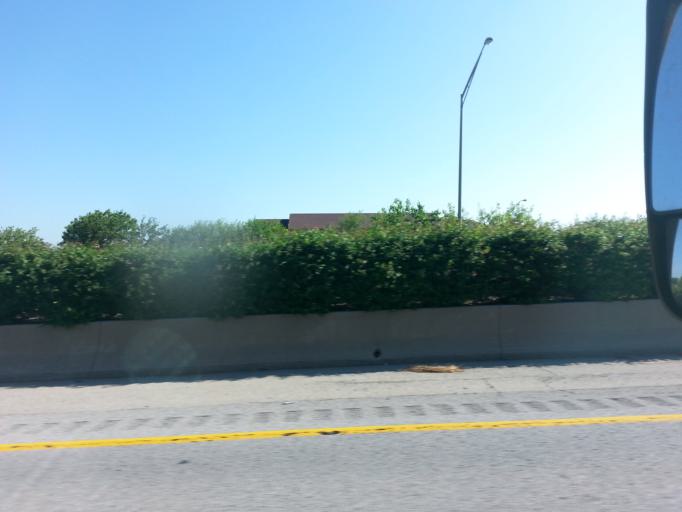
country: US
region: Kentucky
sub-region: Jefferson County
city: Hurstbourne Acres
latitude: 38.2241
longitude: -85.5814
